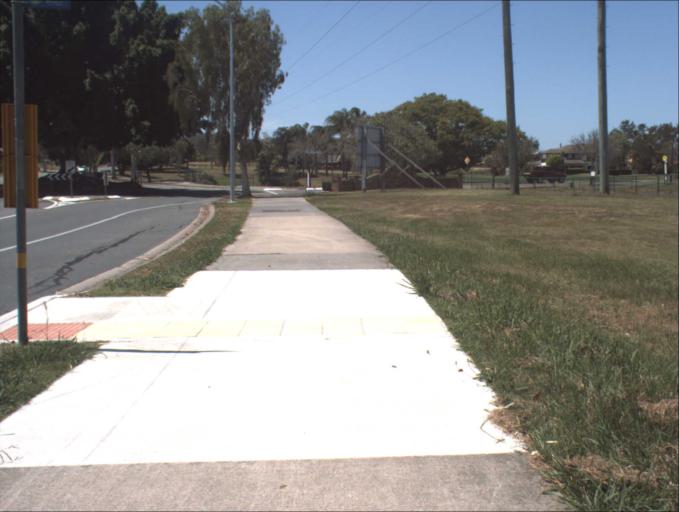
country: AU
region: Queensland
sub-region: Logan
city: Windaroo
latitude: -27.7493
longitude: 153.1911
